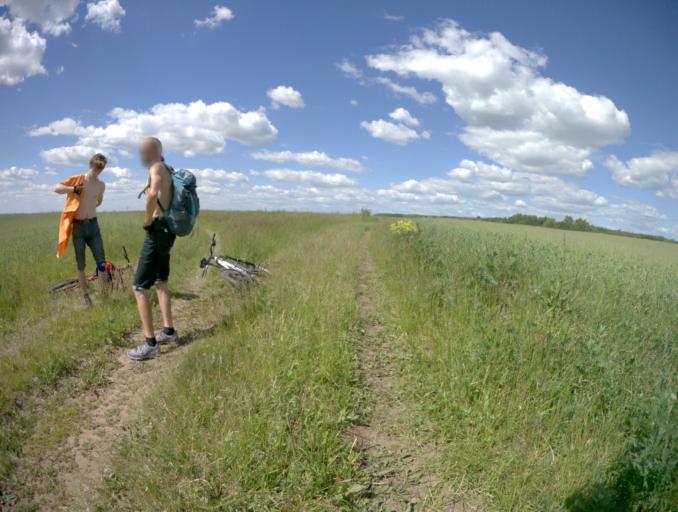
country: RU
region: Vladimir
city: Suzdal'
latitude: 56.2909
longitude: 40.3927
